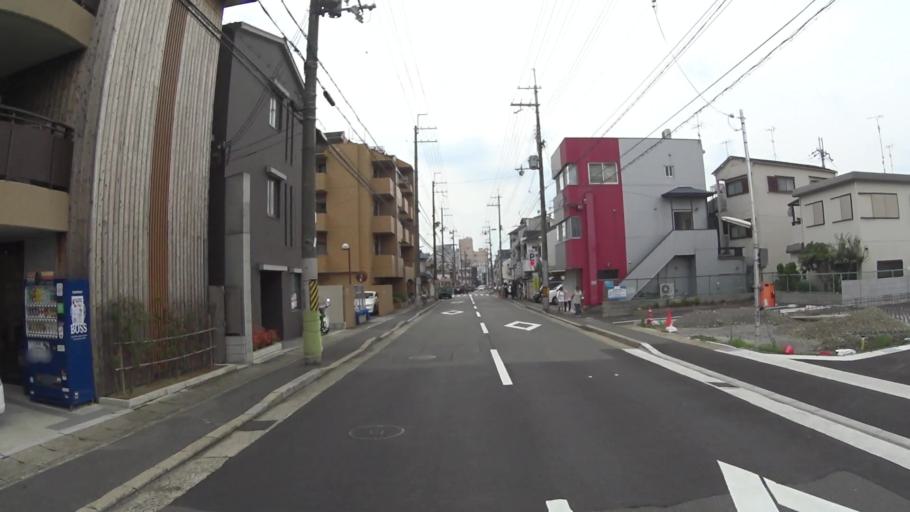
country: JP
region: Kyoto
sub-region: Kyoto-shi
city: Kamigyo-ku
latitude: 35.0477
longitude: 135.7877
